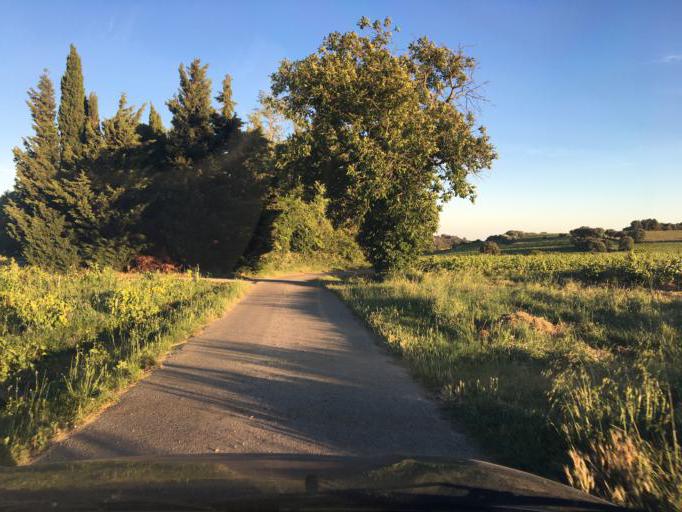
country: FR
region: Provence-Alpes-Cote d'Azur
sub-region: Departement du Vaucluse
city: Chateauneuf-du-Pape
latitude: 44.0809
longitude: 4.8240
